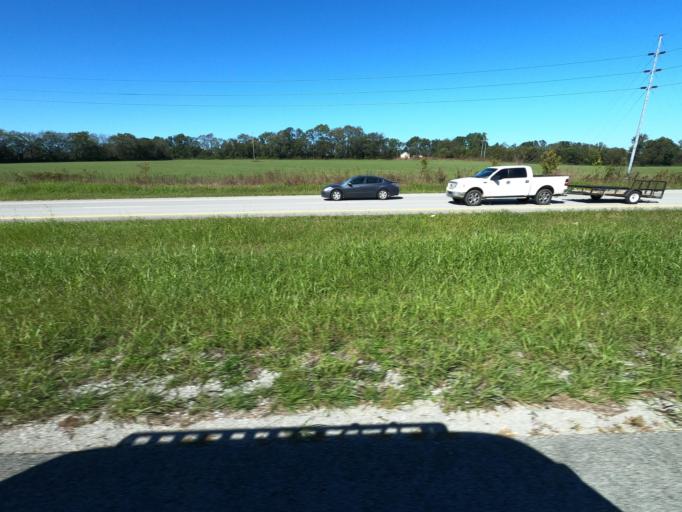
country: US
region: Tennessee
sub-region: Maury County
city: Mount Pleasant
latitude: 35.5545
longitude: -87.2003
